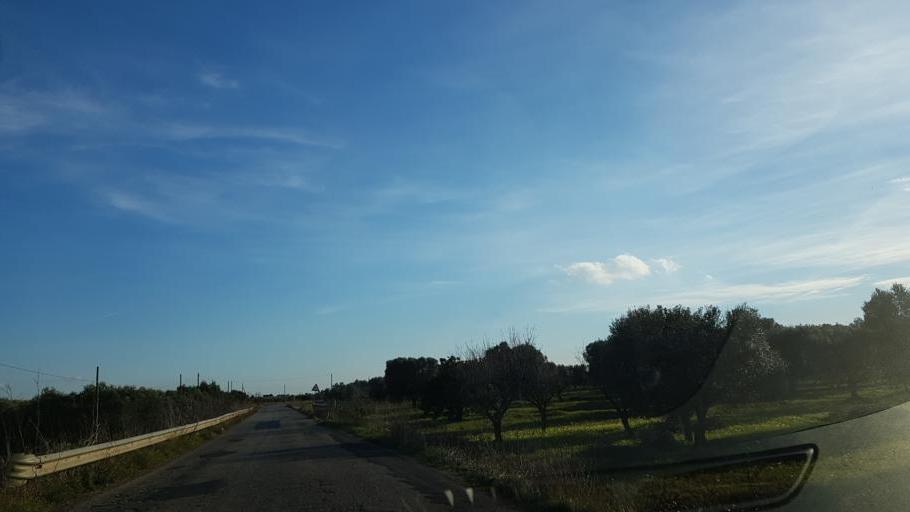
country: IT
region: Apulia
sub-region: Provincia di Brindisi
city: San Vito dei Normanni
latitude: 40.6689
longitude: 17.7795
